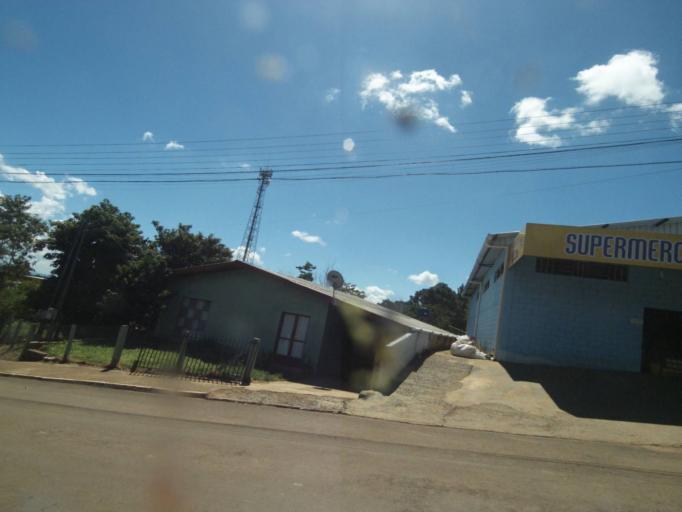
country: BR
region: Parana
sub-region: Pinhao
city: Pinhao
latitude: -25.8344
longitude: -52.0253
